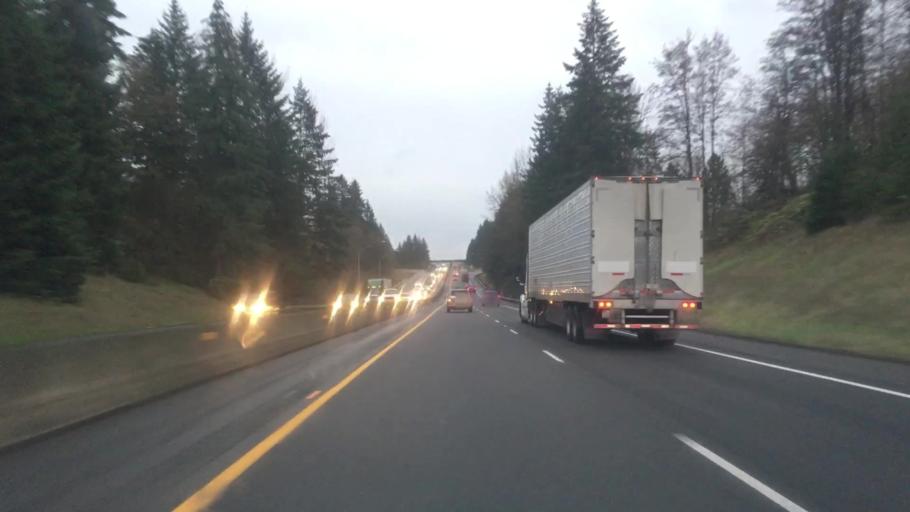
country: US
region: Washington
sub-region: Lewis County
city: Winlock
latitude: 46.4474
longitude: -122.8875
